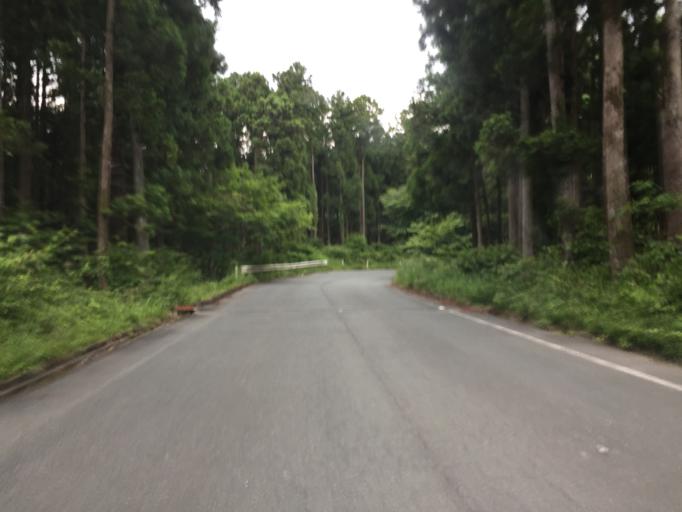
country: JP
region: Miyagi
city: Marumori
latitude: 37.8539
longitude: 140.8727
